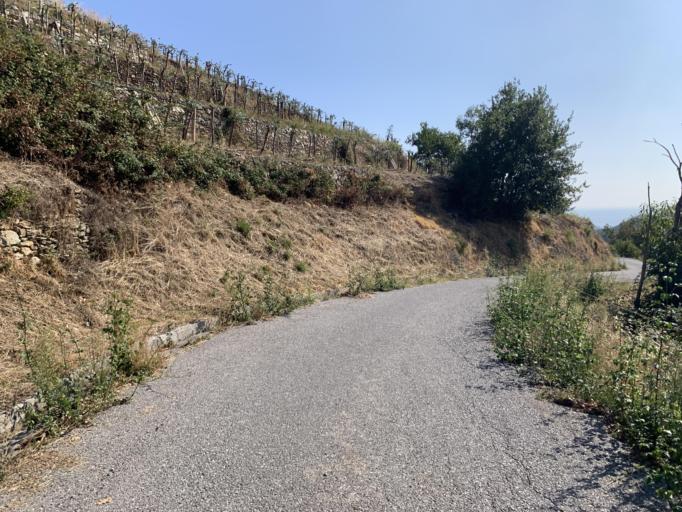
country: IT
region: Liguria
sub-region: Provincia di Savona
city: Magliolo
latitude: 44.1891
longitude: 8.2416
